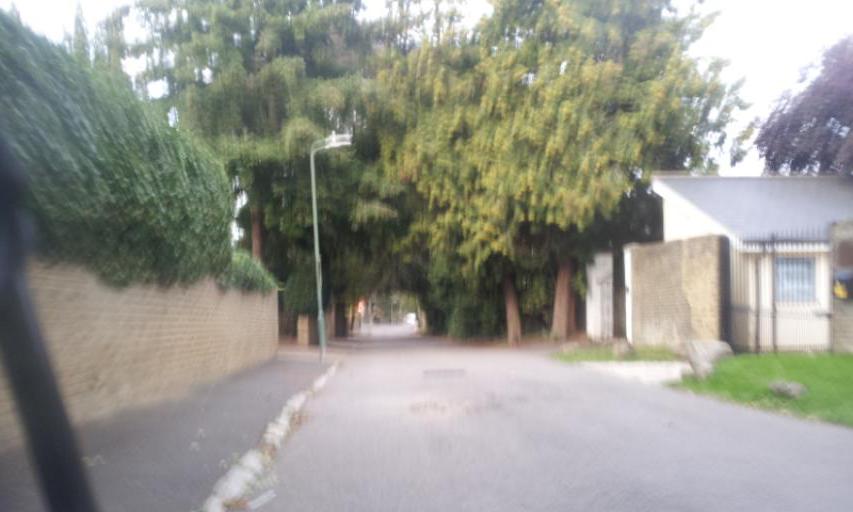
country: GB
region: England
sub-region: Kent
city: Maidstone
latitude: 51.2756
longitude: 0.5073
